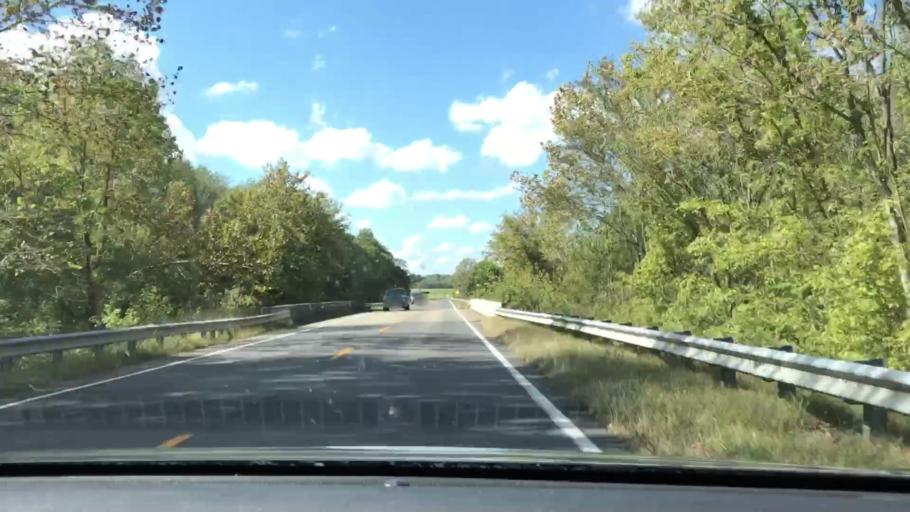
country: US
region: Kentucky
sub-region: McCracken County
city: Reidland
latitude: 36.8849
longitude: -88.5499
